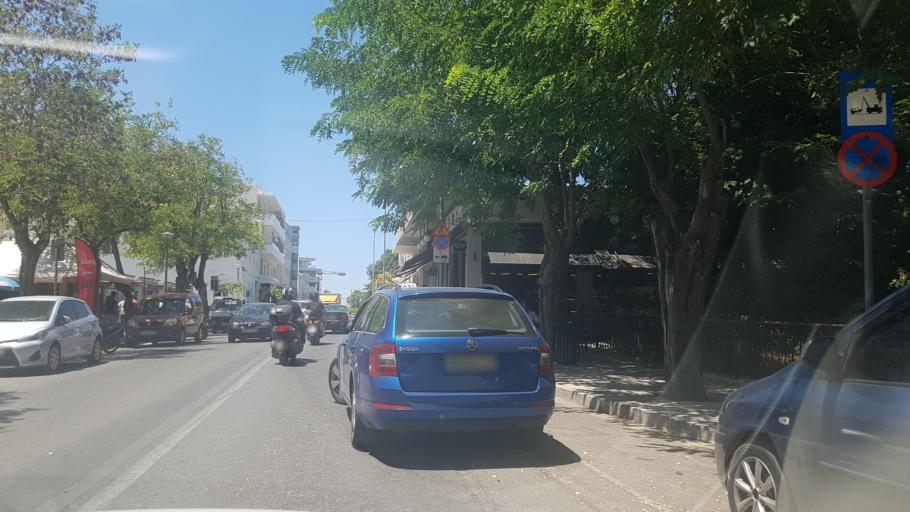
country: GR
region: Crete
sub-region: Nomos Chanias
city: Chania
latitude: 35.5143
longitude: 24.0246
